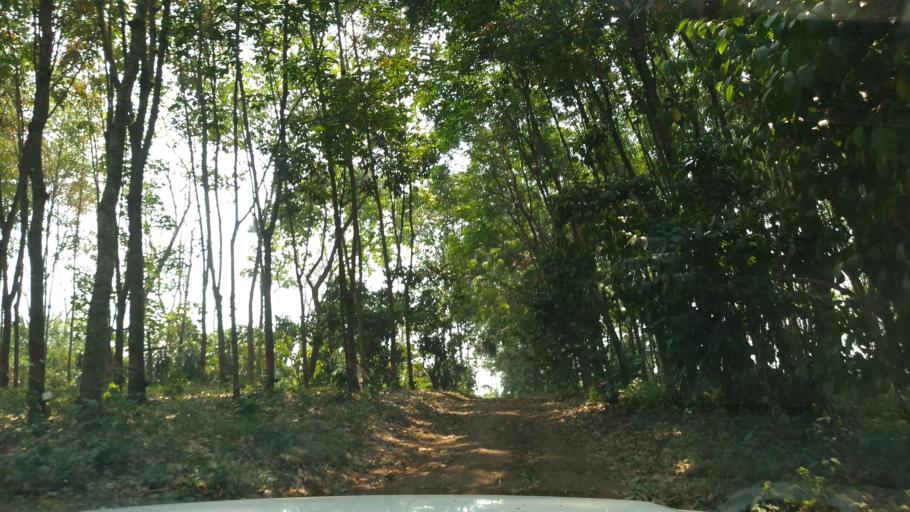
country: MX
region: Veracruz
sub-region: Tezonapa
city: Laguna Chica (Pueblo Nuevo)
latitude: 18.5330
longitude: -96.7605
